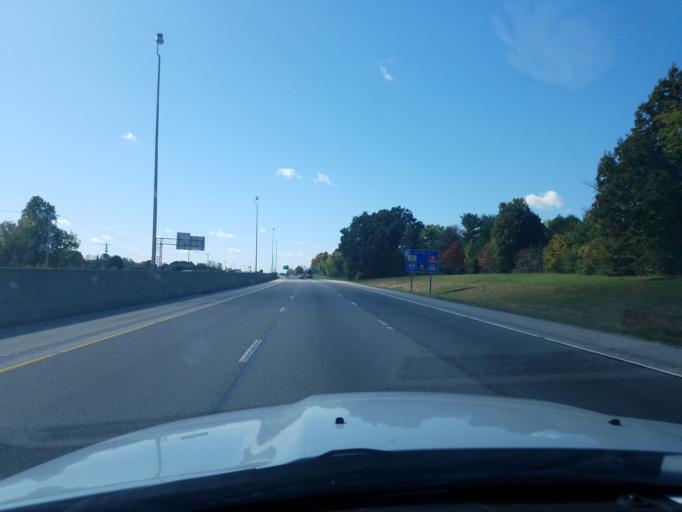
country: US
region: Kentucky
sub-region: Warren County
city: Bowling Green
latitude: 36.9492
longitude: -86.4095
